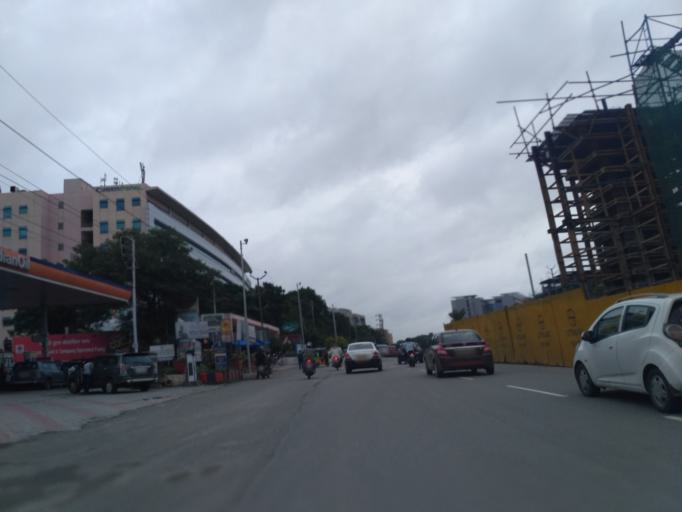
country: IN
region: Telangana
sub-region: Rangareddi
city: Kukatpalli
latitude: 17.4438
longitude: 78.3770
